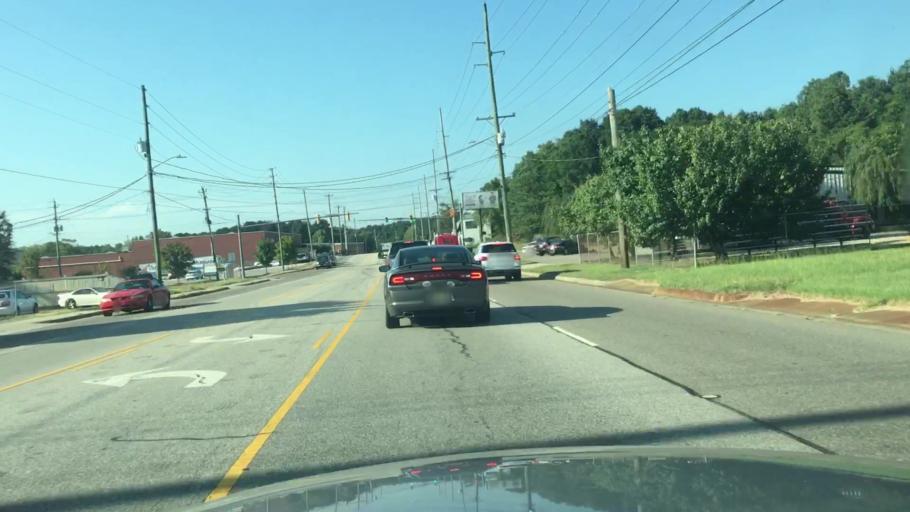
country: US
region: North Carolina
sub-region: Cumberland County
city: Fayetteville
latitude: 35.0497
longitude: -78.8897
